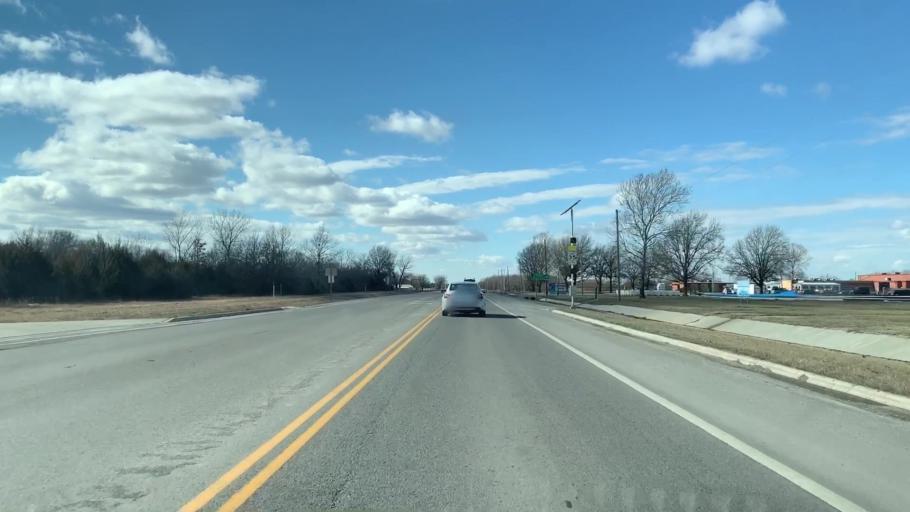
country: US
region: Kansas
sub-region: Crawford County
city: Pittsburg
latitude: 37.3395
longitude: -94.8341
